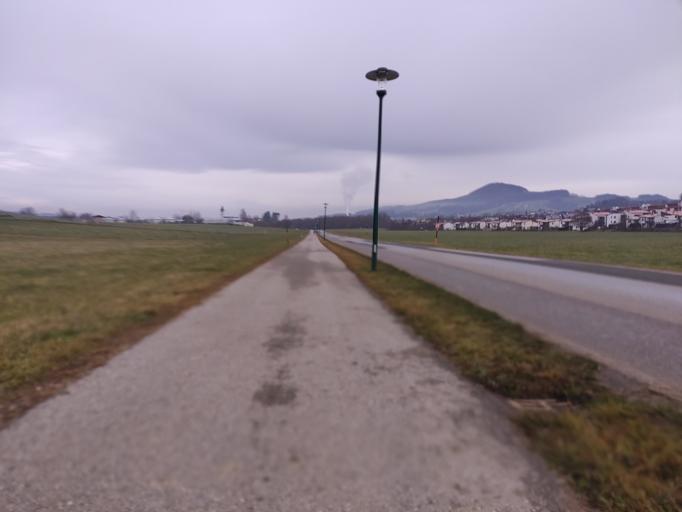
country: AT
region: Salzburg
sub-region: Politischer Bezirk Salzburg-Umgebung
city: Obertrum am See
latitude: 47.9282
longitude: 13.0745
